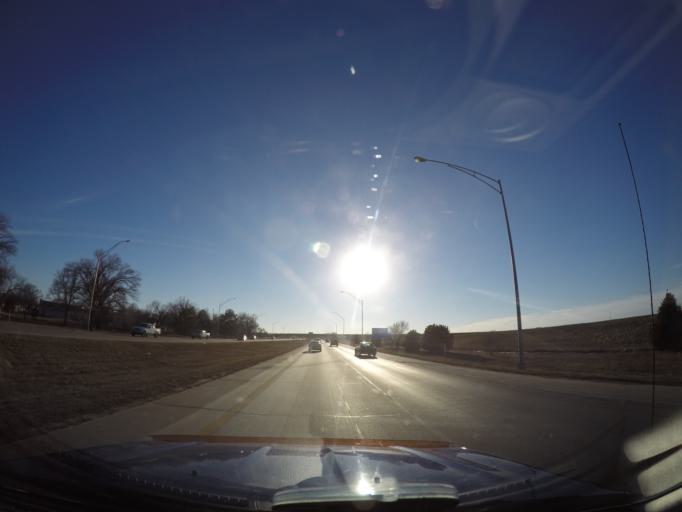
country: US
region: Kansas
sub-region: Sedgwick County
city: Wichita
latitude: 37.7107
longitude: -97.4034
